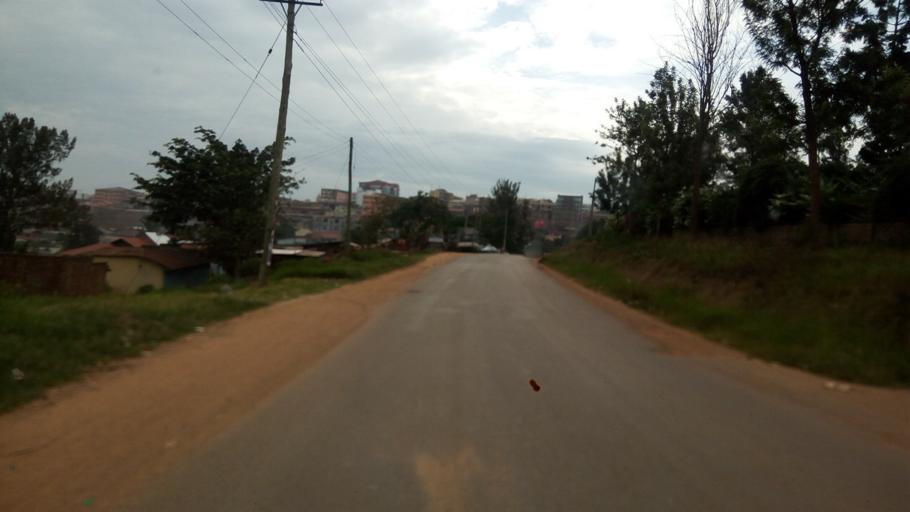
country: UG
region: Western Region
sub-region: Mbarara District
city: Mbarara
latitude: -0.6051
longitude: 30.6562
